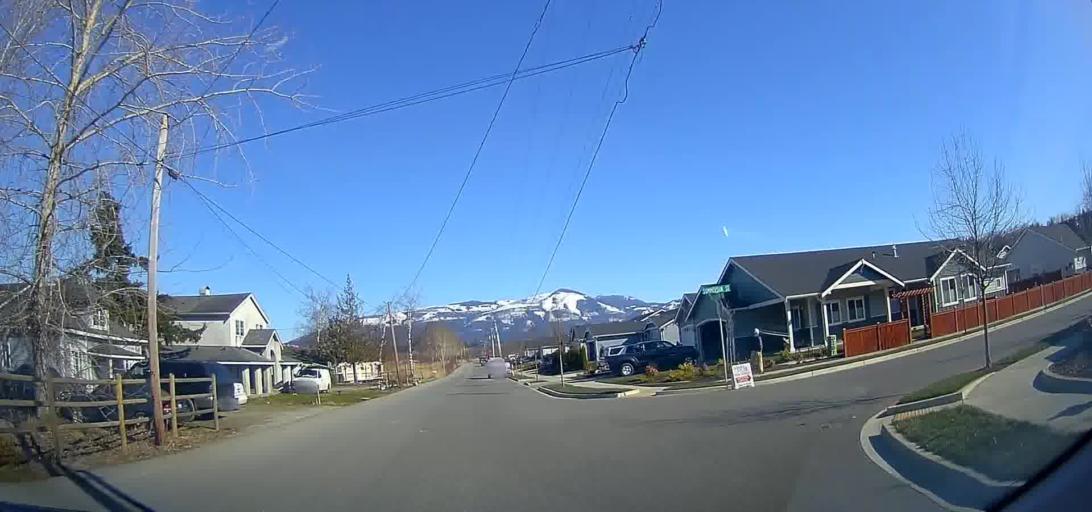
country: US
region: Washington
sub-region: Skagit County
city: Mount Vernon
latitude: 48.4390
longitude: -122.2898
